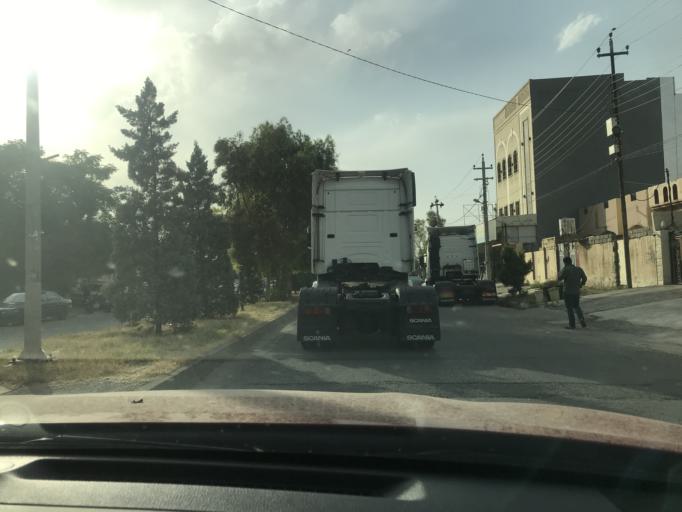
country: IQ
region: Arbil
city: Erbil
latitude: 36.1787
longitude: 43.9790
